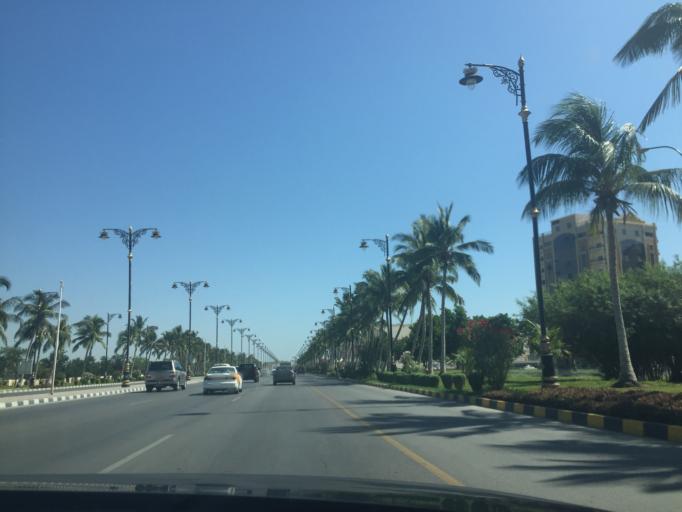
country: OM
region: Zufar
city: Salalah
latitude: 17.0239
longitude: 54.0949
